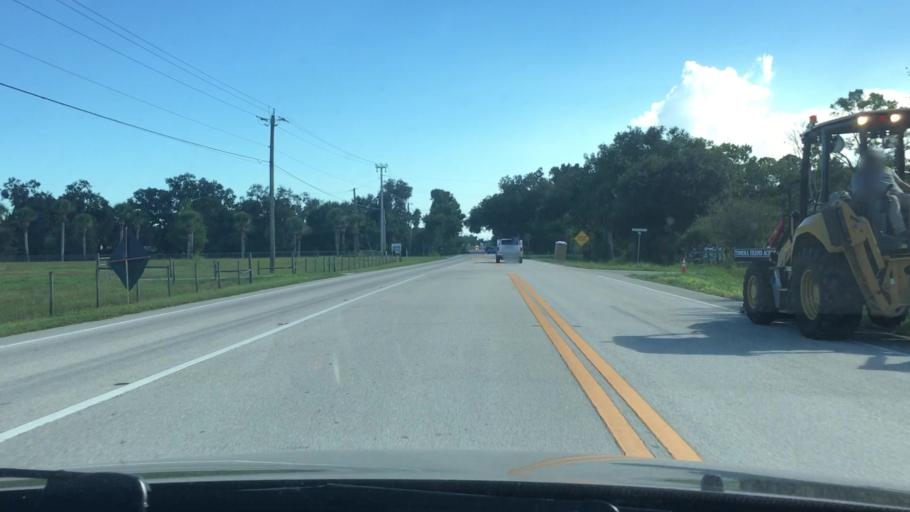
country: US
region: Florida
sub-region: Volusia County
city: Samsula-Spruce Creek
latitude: 29.0897
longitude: -81.0686
